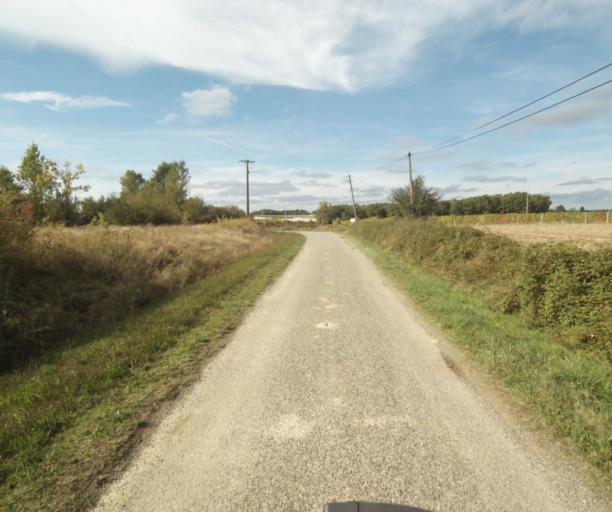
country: FR
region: Midi-Pyrenees
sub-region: Departement du Tarn-et-Garonne
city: Saint-Porquier
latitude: 43.9453
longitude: 1.1368
